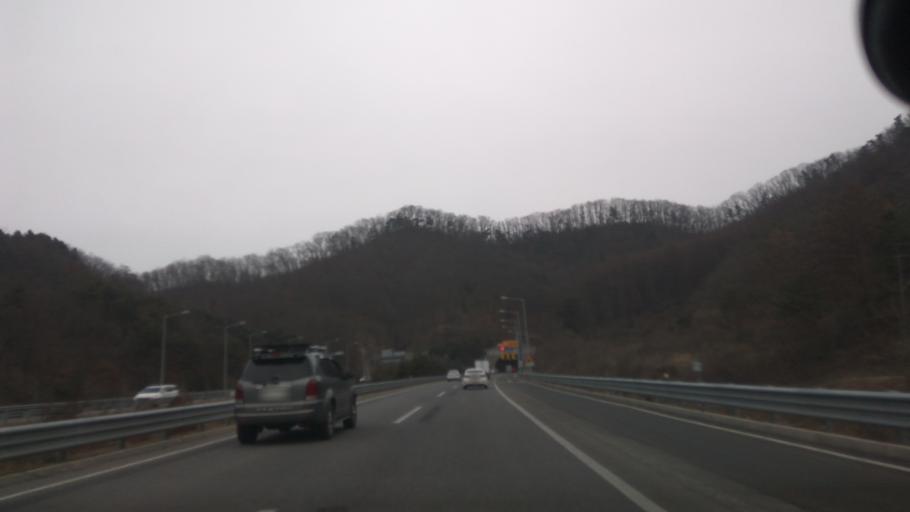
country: KR
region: Gangwon-do
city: Sindong
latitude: 37.7395
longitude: 127.6388
